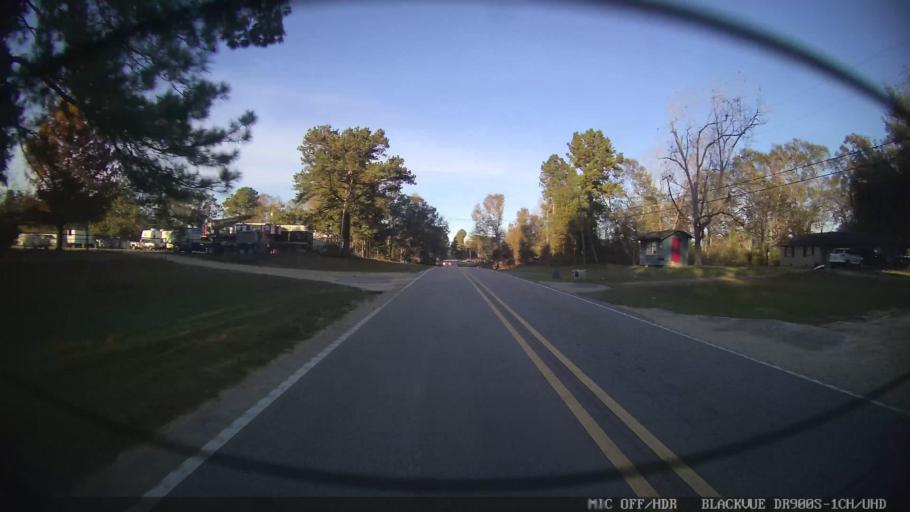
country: US
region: Mississippi
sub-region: Lamar County
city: Lumberton
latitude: 31.0471
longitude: -89.4344
